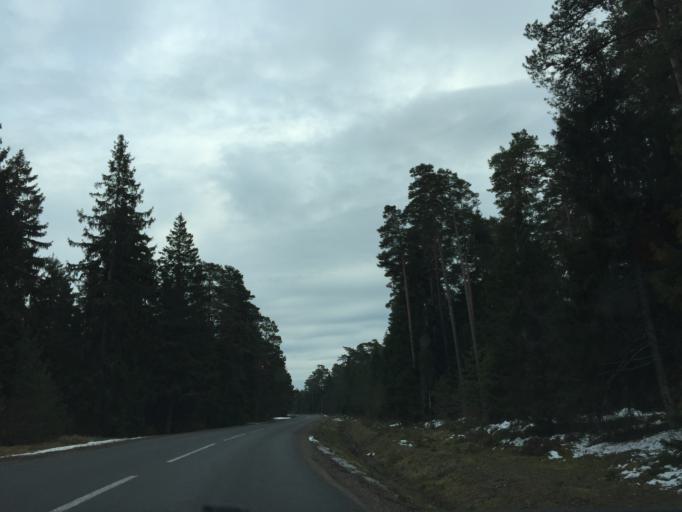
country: EE
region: Saare
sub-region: Kuressaare linn
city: Kuressaare
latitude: 58.4337
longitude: 22.0673
